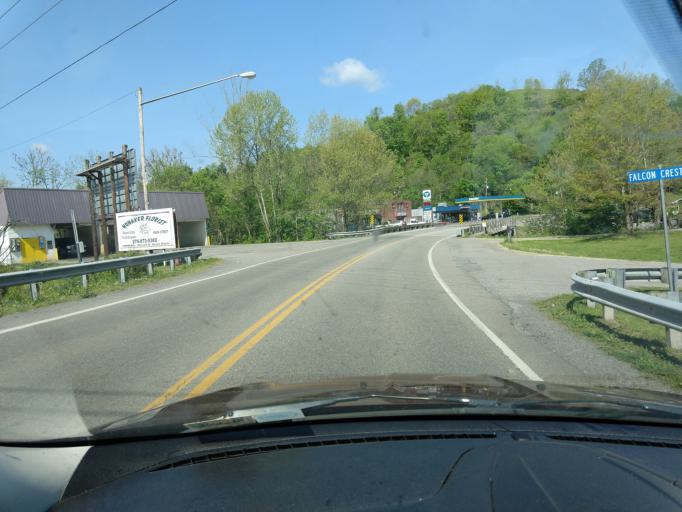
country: US
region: Virginia
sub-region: Russell County
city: Honaker
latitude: 37.0135
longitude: -81.9685
